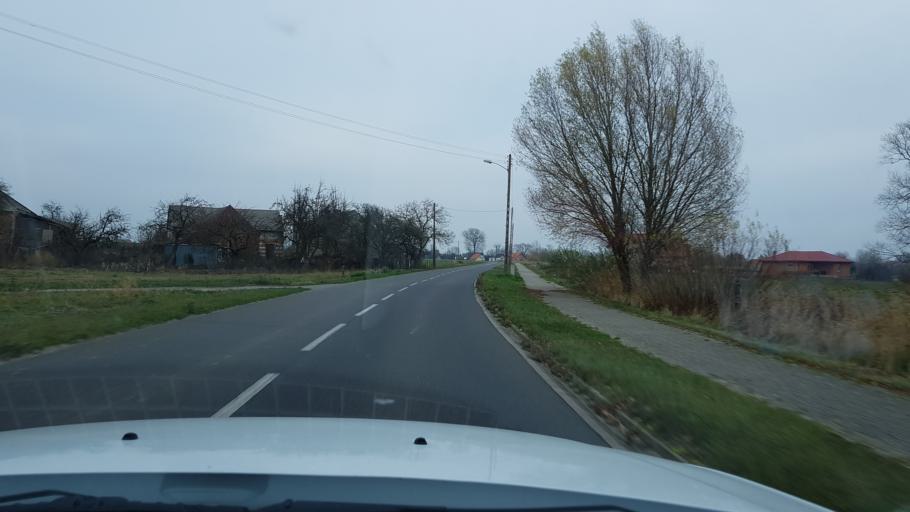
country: PL
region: West Pomeranian Voivodeship
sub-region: Powiat kamienski
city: Kamien Pomorski
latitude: 53.9768
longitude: 14.6892
